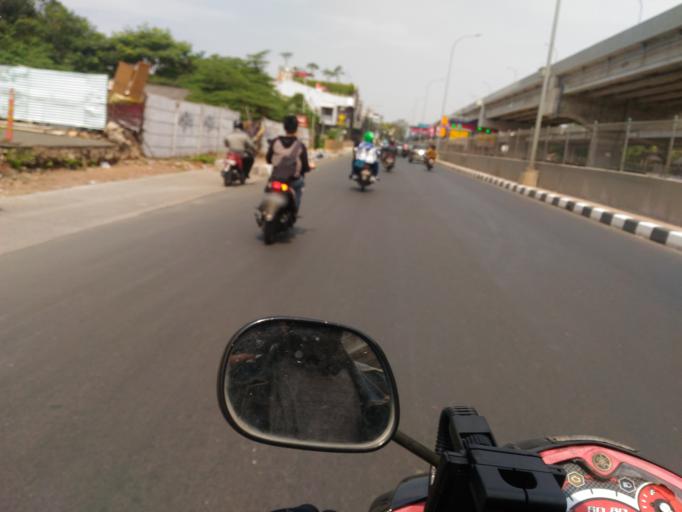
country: ID
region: West Java
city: Bekasi
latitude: -6.2484
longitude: 106.9318
